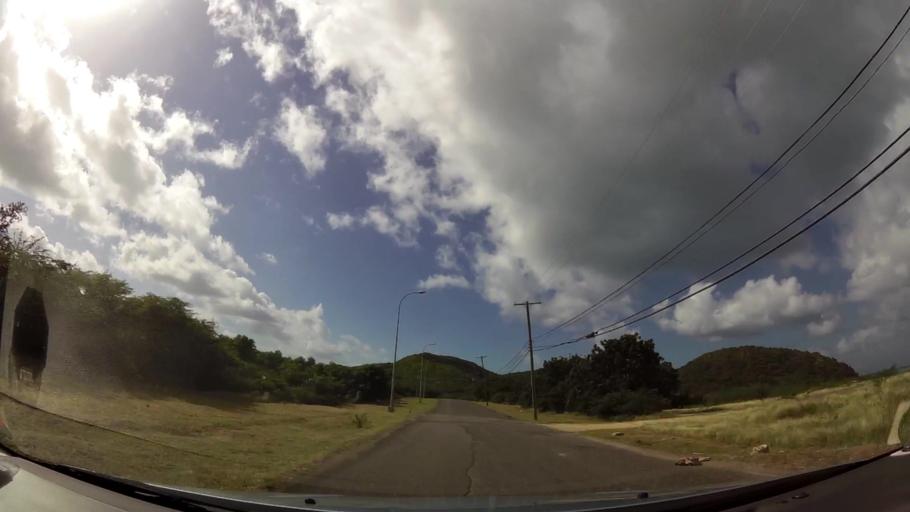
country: AG
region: Saint John
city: Saint John's
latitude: 17.1179
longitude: -61.8663
